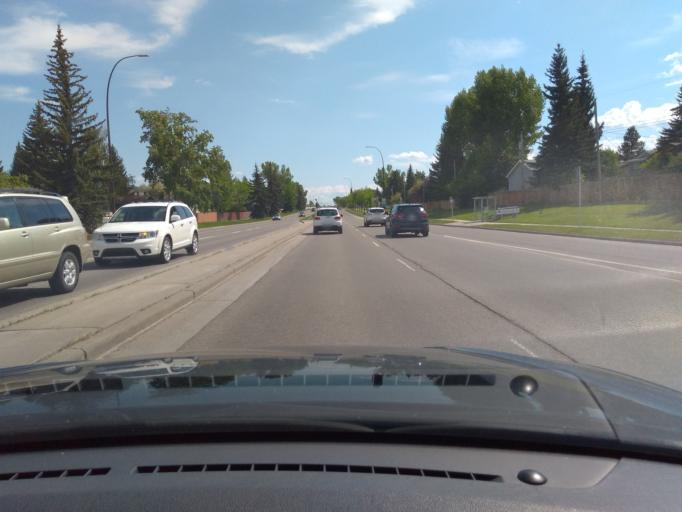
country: CA
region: Alberta
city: Calgary
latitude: 50.9610
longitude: -114.1181
